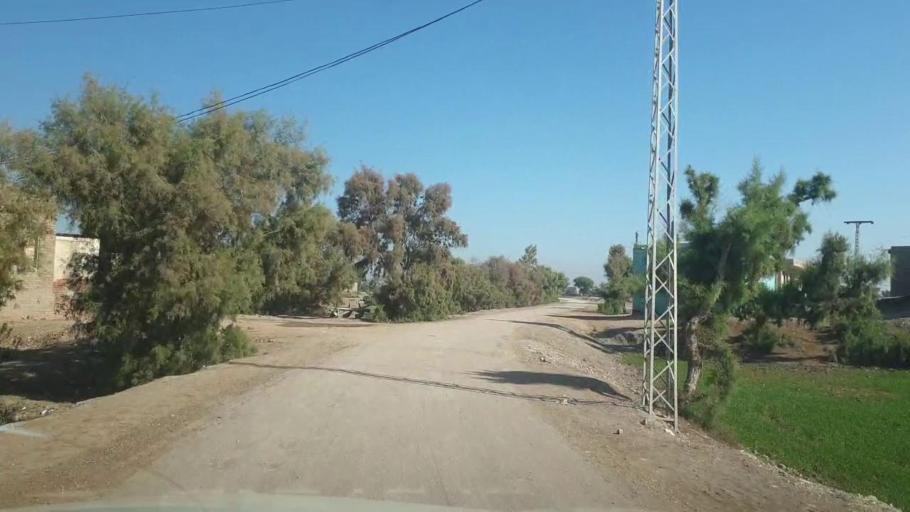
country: PK
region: Sindh
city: Bhan
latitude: 26.5252
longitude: 67.6424
